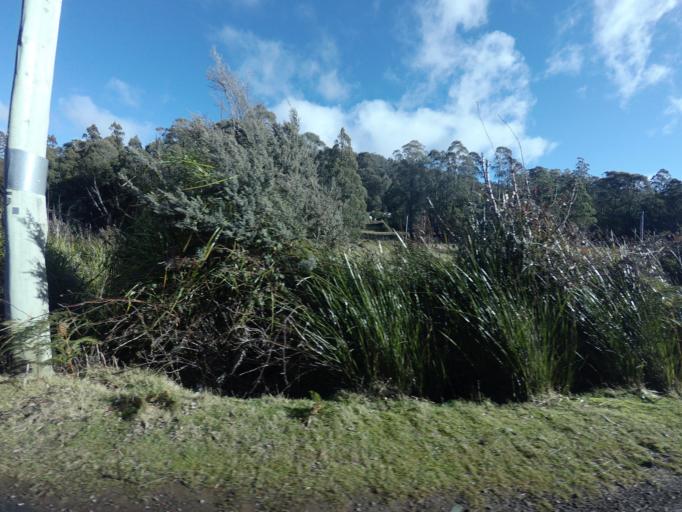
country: AU
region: Tasmania
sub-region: Glenorchy
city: Berriedale
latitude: -42.8451
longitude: 147.1667
